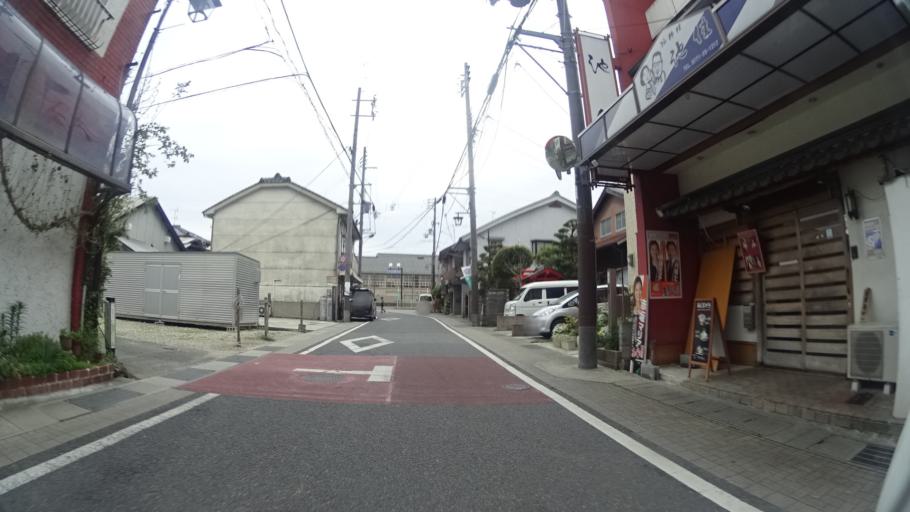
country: JP
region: Kyoto
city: Kameoka
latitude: 35.0130
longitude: 135.5788
